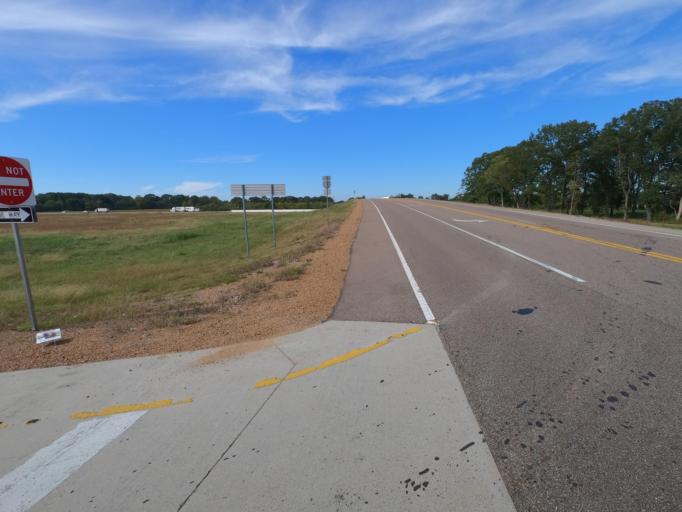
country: US
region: Tennessee
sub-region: Fayette County
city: Hickory Withe
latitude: 35.2906
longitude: -89.6084
